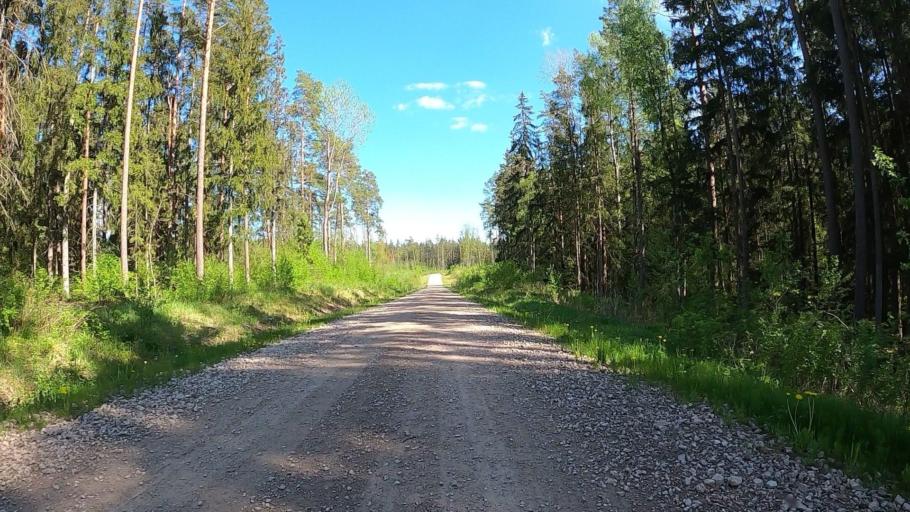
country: LV
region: Baldone
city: Baldone
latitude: 56.7904
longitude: 24.3357
